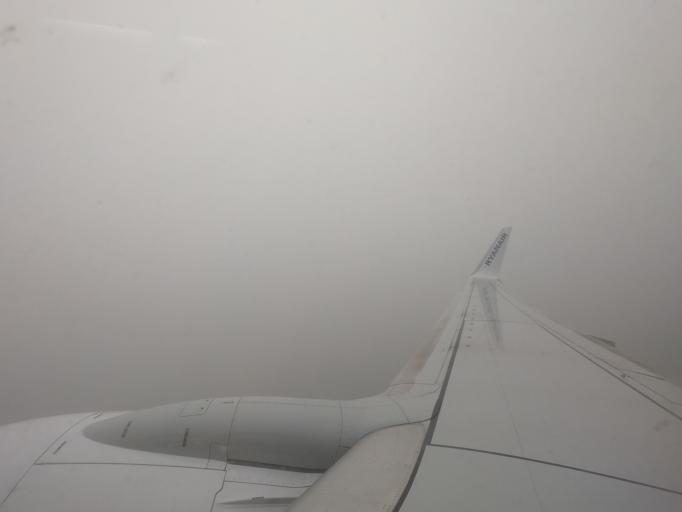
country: DE
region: Hesse
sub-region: Regierungsbezirk Darmstadt
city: Buttelborn
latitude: 49.9392
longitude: 8.5304
